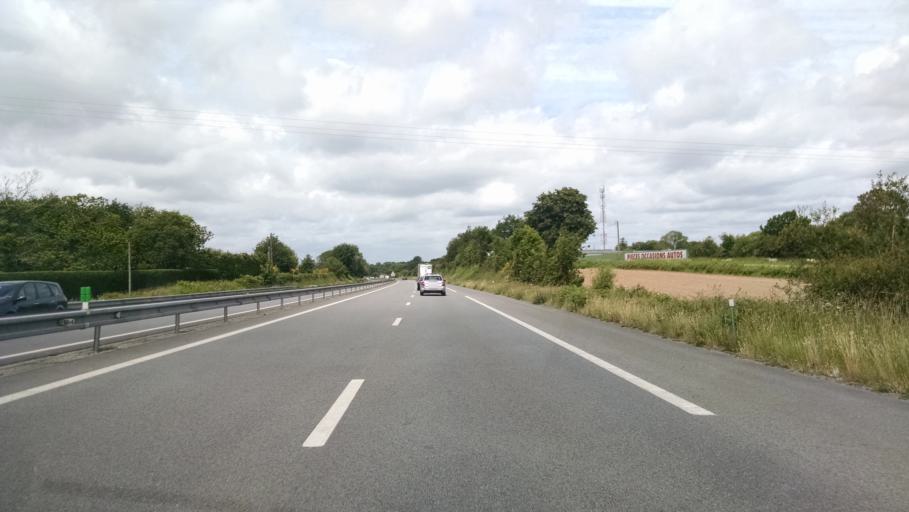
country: FR
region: Brittany
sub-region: Departement du Morbihan
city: Brech
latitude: 47.6977
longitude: -3.0382
